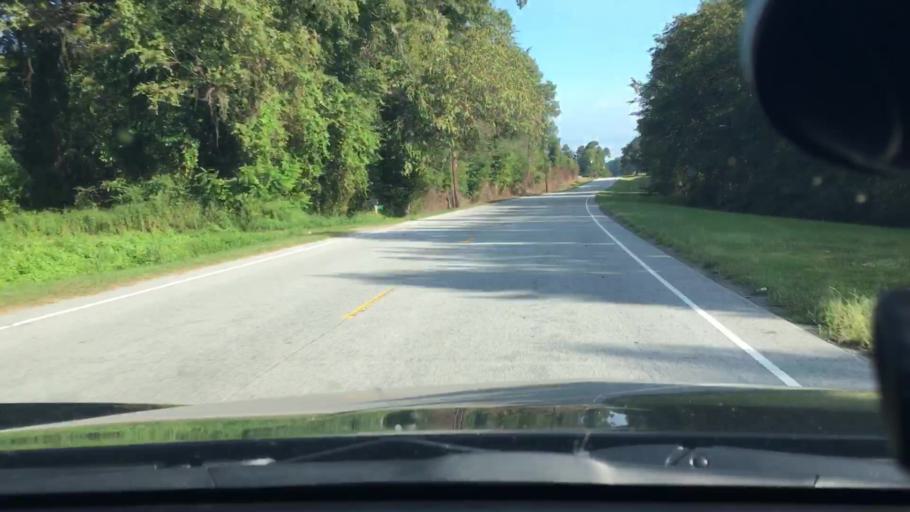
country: US
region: North Carolina
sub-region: Edgecombe County
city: Pinetops
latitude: 35.7230
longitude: -77.5304
